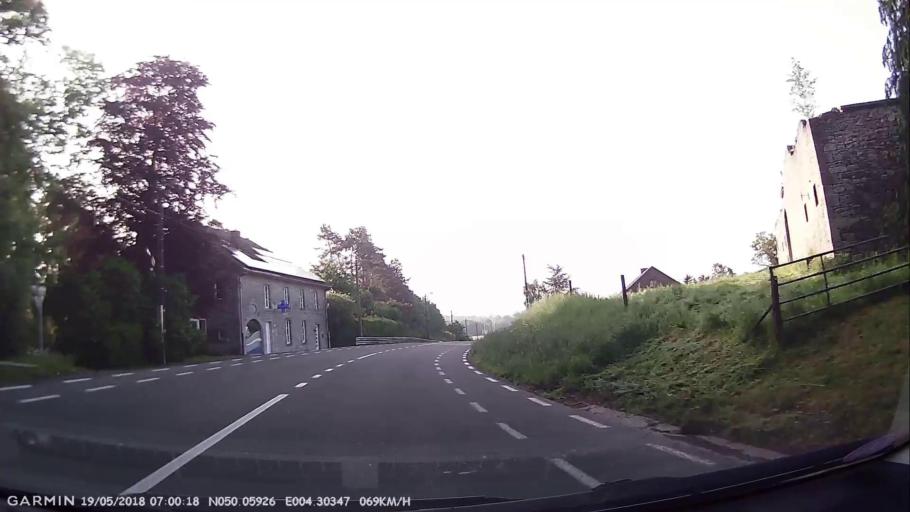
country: BE
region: Wallonia
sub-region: Province du Hainaut
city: Chimay
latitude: 50.0592
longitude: 4.3037
